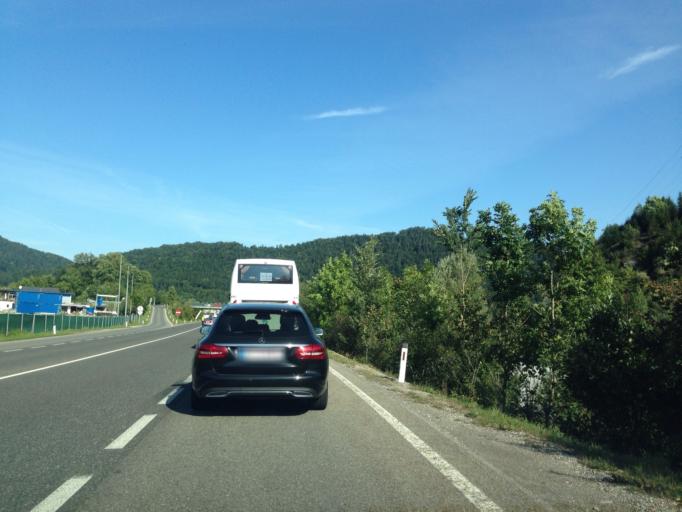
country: AT
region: Tyrol
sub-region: Politischer Bezirk Reutte
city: Musau
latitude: 47.5461
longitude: 10.6620
